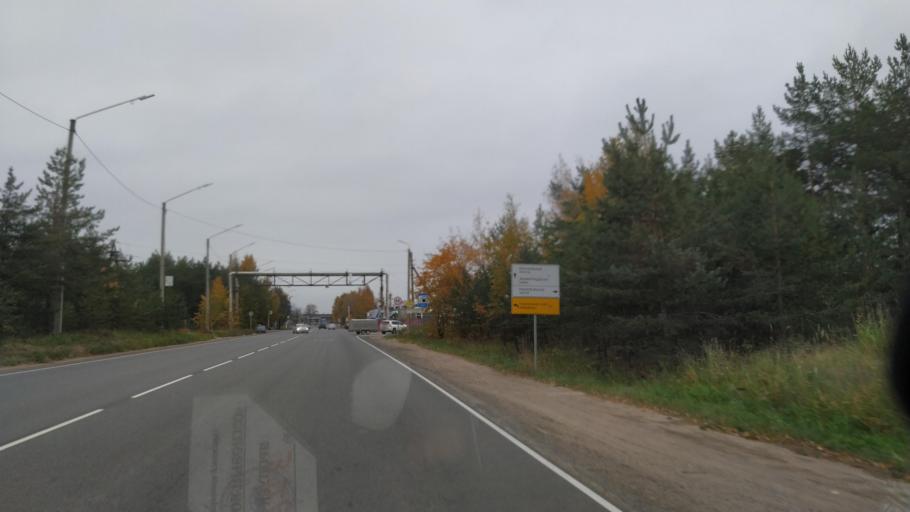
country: RU
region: Leningrad
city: Sosnovyy Bor
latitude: 59.8745
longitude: 29.0884
